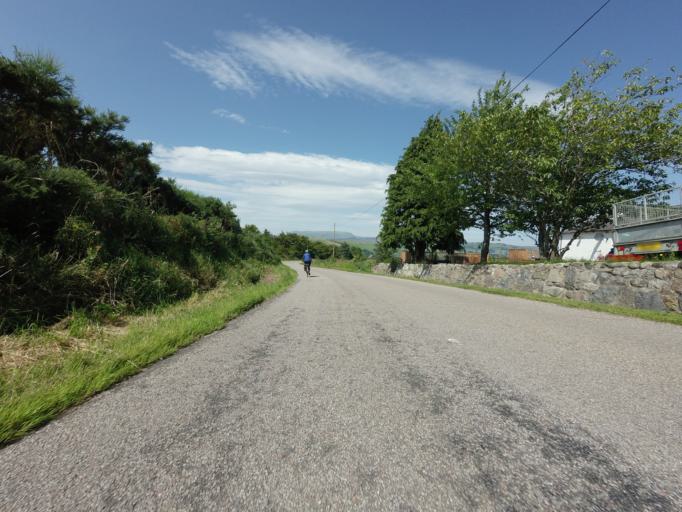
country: GB
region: Scotland
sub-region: Highland
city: Conon Bridge
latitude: 57.5634
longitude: -4.4199
